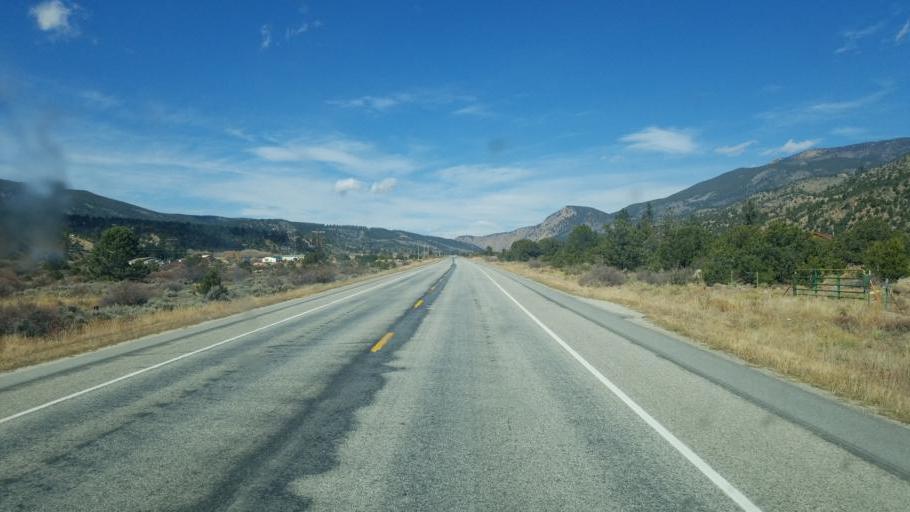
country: US
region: Colorado
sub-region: Chaffee County
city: Buena Vista
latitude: 38.9418
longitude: -106.1910
